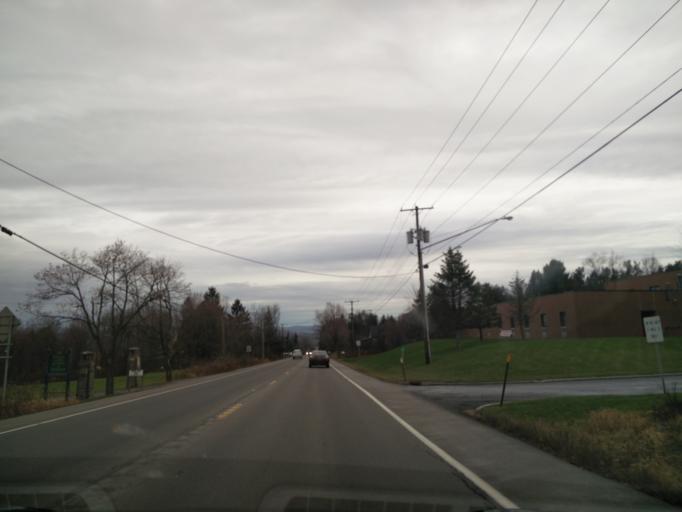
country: US
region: New York
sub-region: Tompkins County
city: Northwest Ithaca
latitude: 42.4640
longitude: -76.5355
